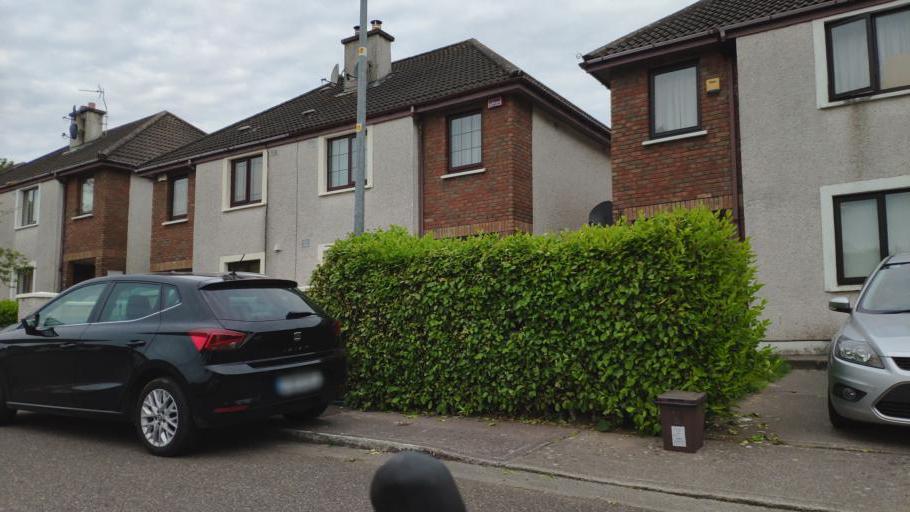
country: IE
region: Munster
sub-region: County Cork
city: Cork
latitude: 51.9112
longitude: -8.4566
